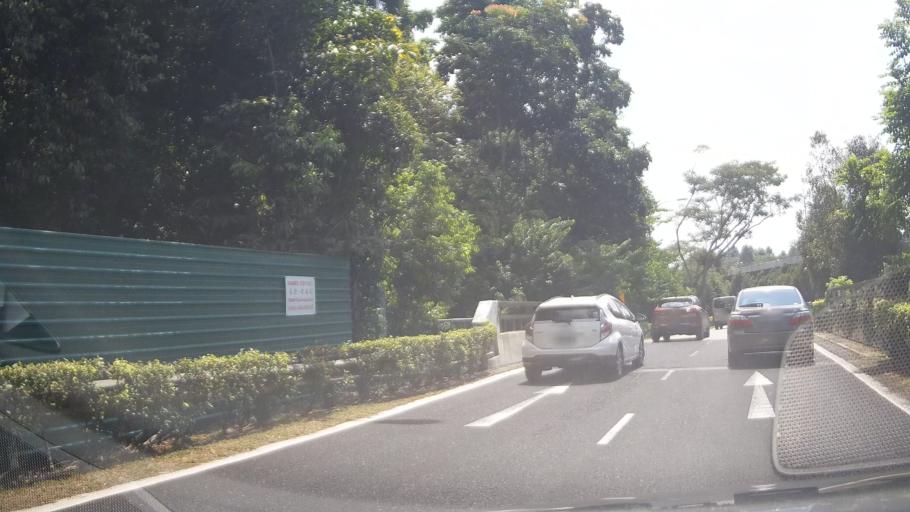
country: SG
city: Singapore
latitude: 1.3426
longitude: 103.7794
